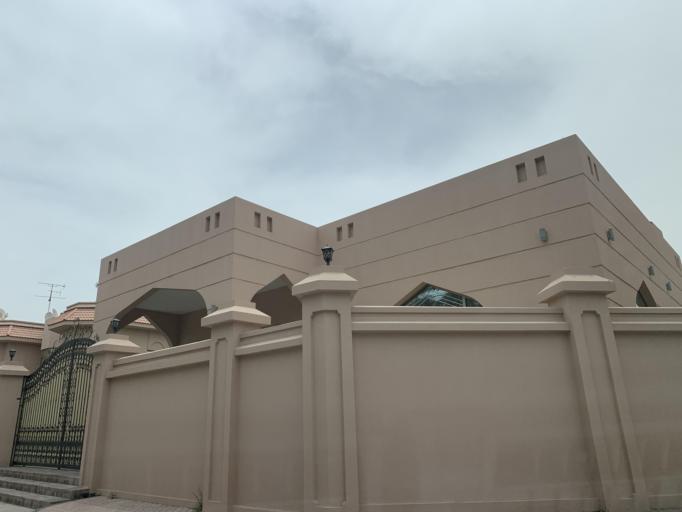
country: BH
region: Northern
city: Ar Rifa'
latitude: 26.1397
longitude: 50.5504
